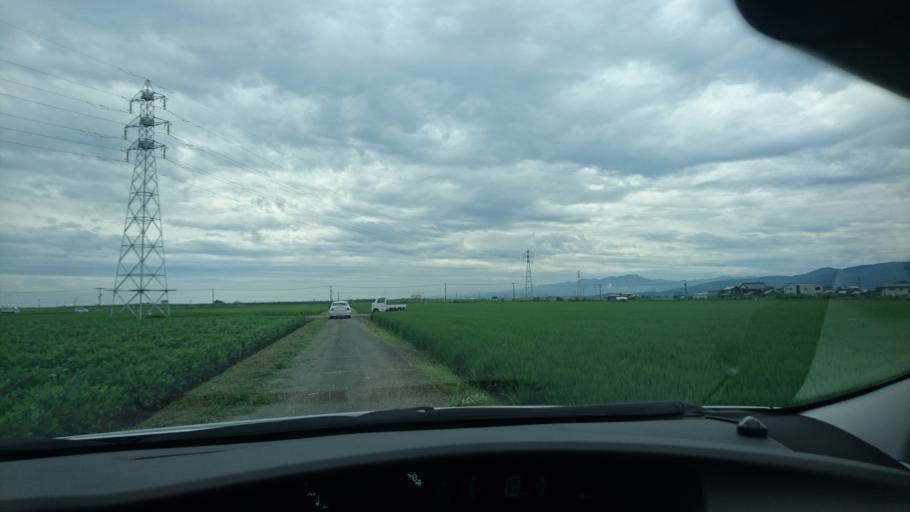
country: JP
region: Saga Prefecture
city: Takeocho-takeo
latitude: 33.2121
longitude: 130.1261
